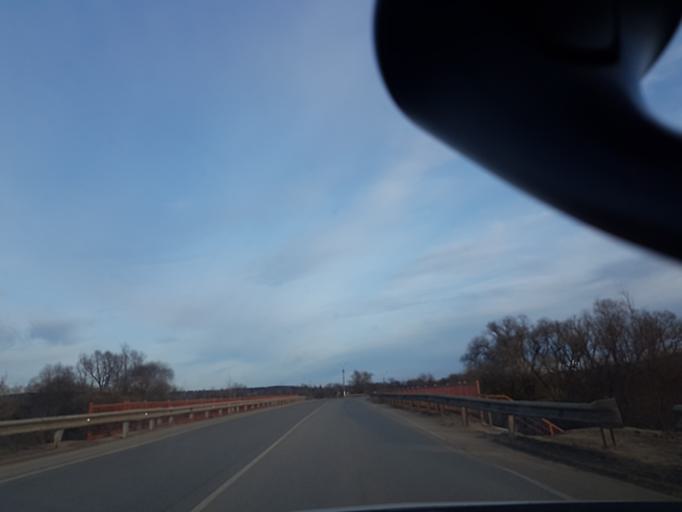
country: RU
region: Moskovskaya
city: Istra
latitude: 55.8936
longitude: 36.8646
